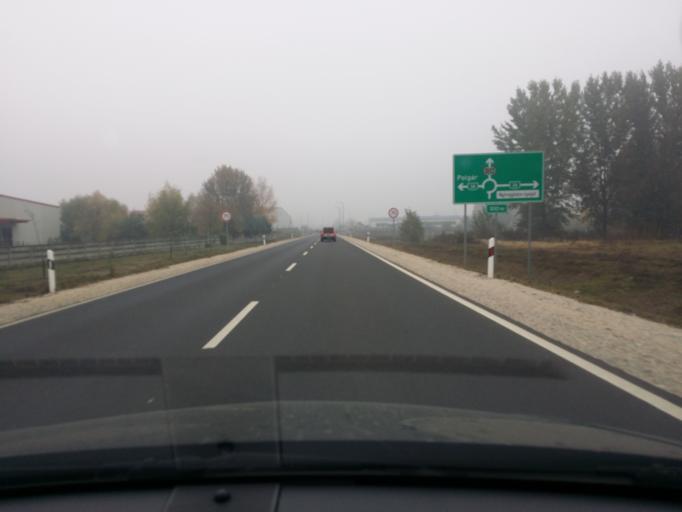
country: HU
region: Szabolcs-Szatmar-Bereg
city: Nyiregyhaza
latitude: 47.9539
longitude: 21.6554
